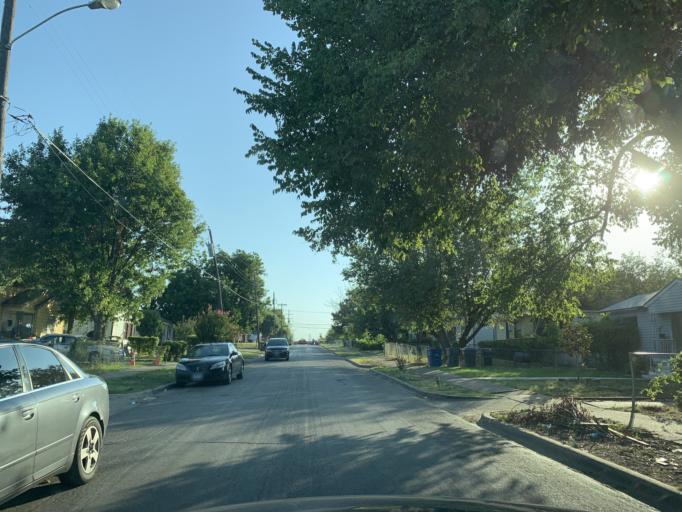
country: US
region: Texas
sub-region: Dallas County
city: Dallas
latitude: 32.7084
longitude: -96.7958
